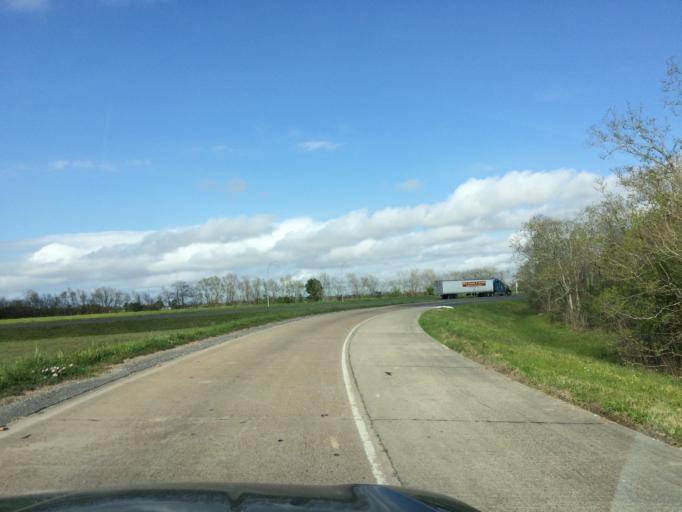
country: US
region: Louisiana
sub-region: Jefferson Davis Parish
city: Welsh
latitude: 30.2457
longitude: -92.8205
